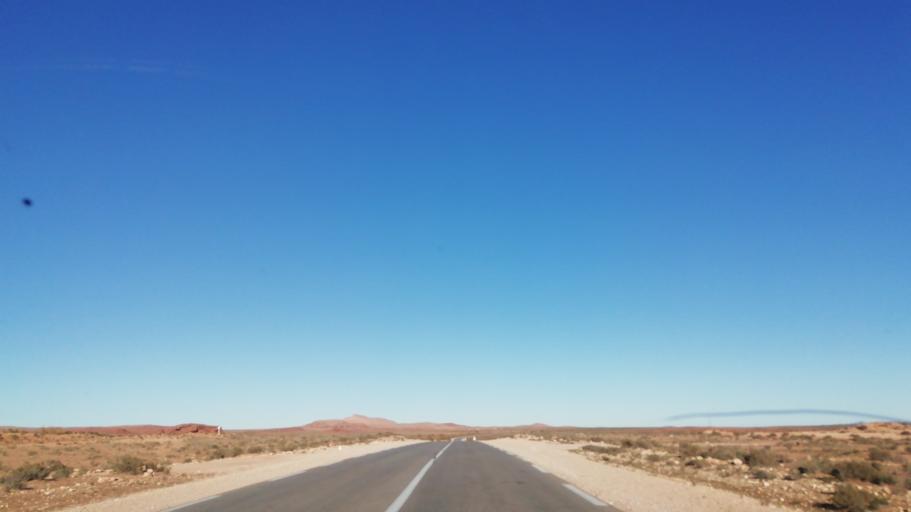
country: DZ
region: El Bayadh
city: El Abiodh Sidi Cheikh
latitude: 33.1055
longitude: 0.2160
